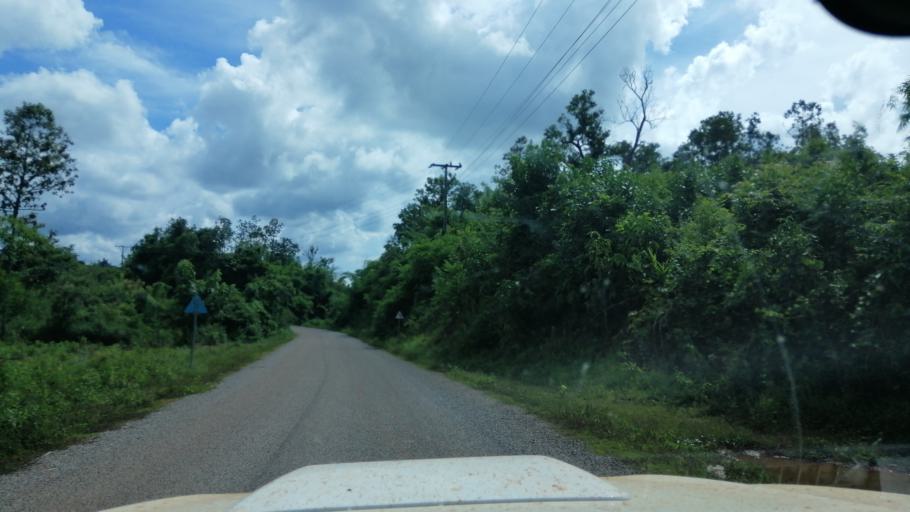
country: TH
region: Nan
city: Mae Charim
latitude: 18.3856
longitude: 101.1553
